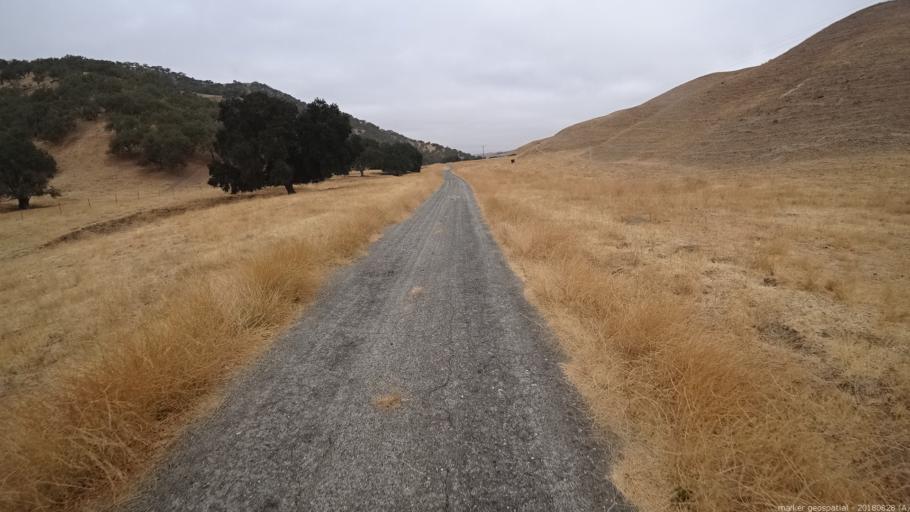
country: US
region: California
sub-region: San Luis Obispo County
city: San Miguel
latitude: 35.9402
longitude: -120.7513
